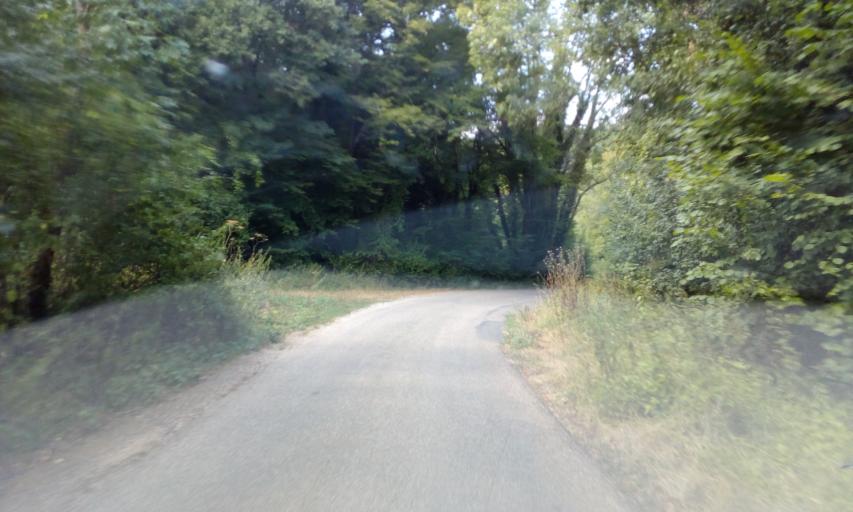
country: FR
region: Lorraine
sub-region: Departement de Meurthe-et-Moselle
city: Pagny-sur-Moselle
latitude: 48.9508
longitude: 5.9089
